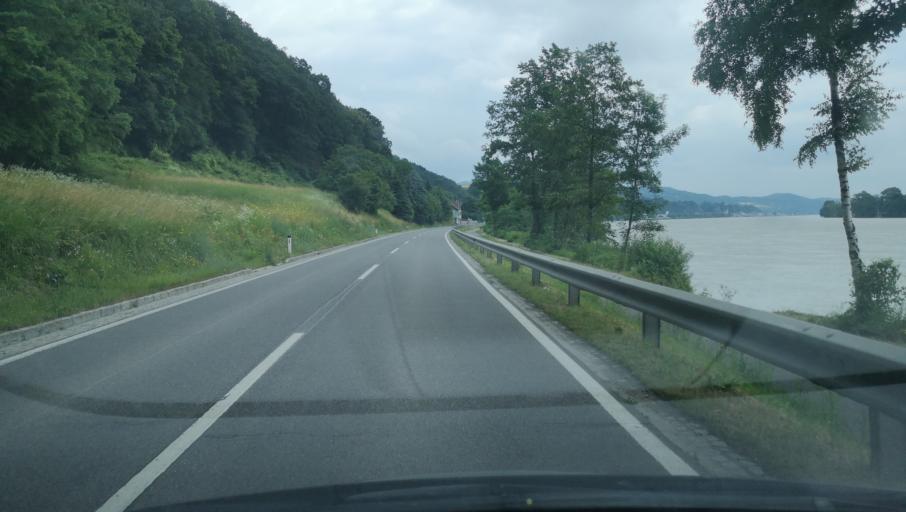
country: AT
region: Lower Austria
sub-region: Politischer Bezirk Melk
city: Marbach an der Donau
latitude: 48.2063
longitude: 15.1164
